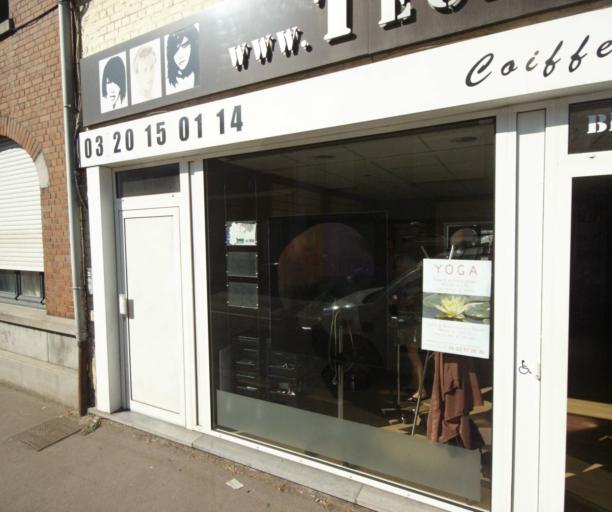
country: FR
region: Nord-Pas-de-Calais
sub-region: Departement du Nord
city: Wervicq-Sud
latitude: 50.7712
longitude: 3.0461
